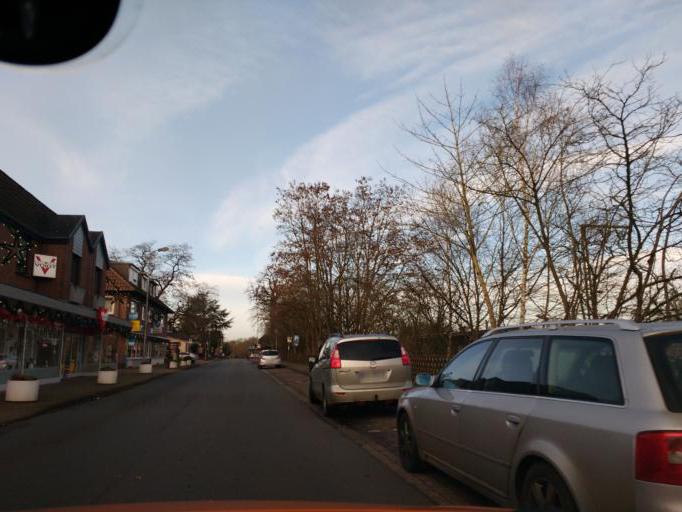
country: DE
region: Lower Saxony
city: Hude
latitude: 53.1088
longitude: 8.4611
